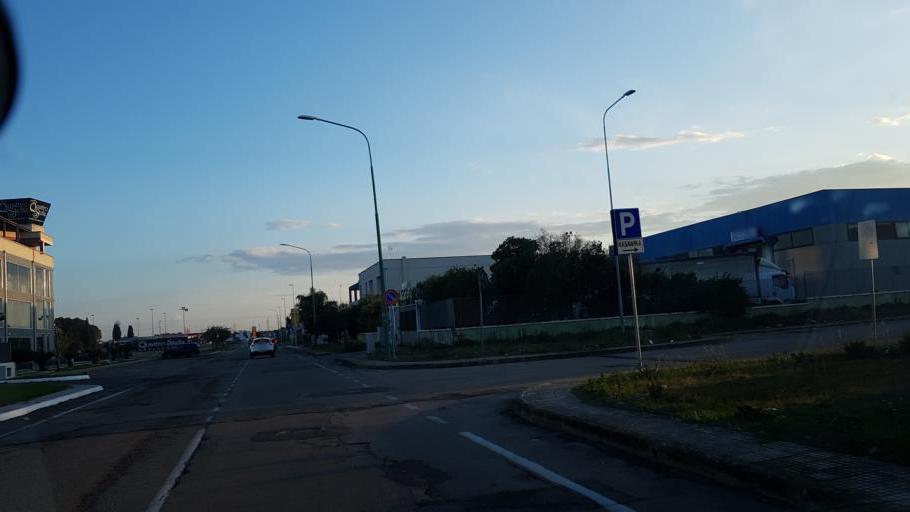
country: IT
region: Apulia
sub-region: Provincia di Lecce
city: Giorgilorio
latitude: 40.3804
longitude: 18.1394
